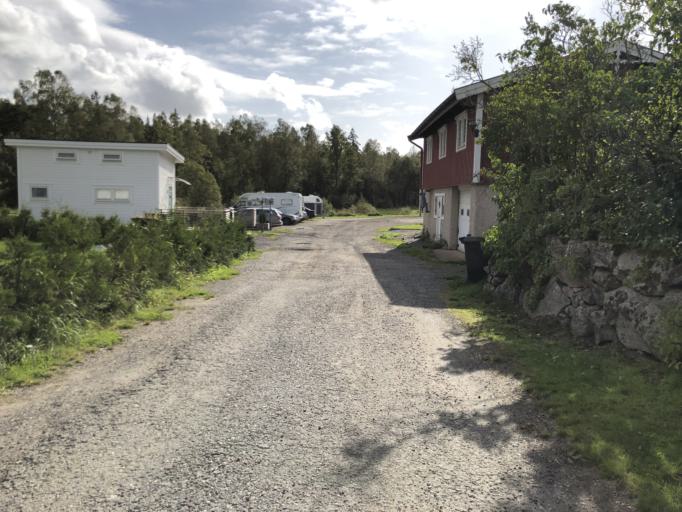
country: SE
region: Vaestra Goetaland
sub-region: Goteborg
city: Majorna
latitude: 57.7488
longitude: 11.8608
